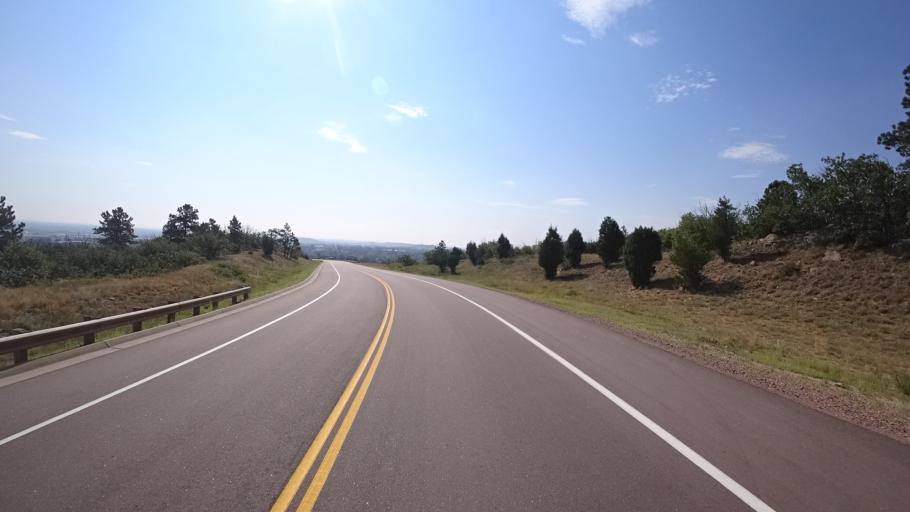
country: US
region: Colorado
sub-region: El Paso County
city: Fort Carson
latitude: 38.7469
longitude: -104.8163
